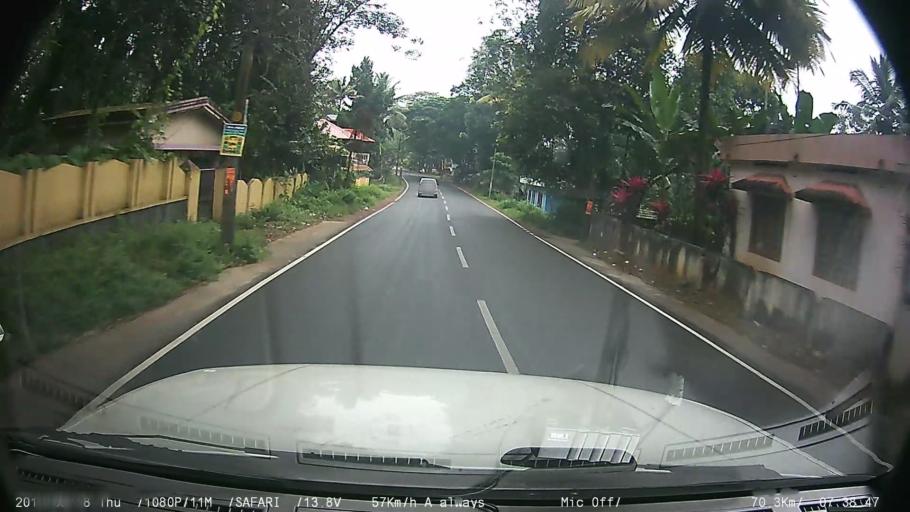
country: IN
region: Kerala
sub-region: Kottayam
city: Changanacheri
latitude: 9.4414
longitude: 76.5692
